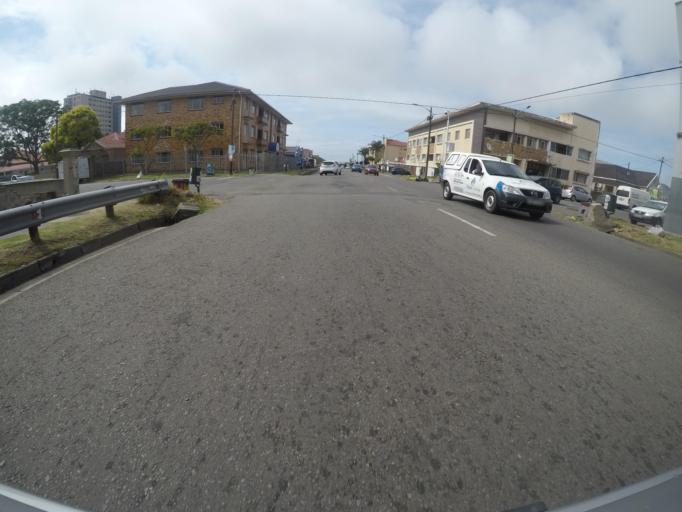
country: ZA
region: Eastern Cape
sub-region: Buffalo City Metropolitan Municipality
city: East London
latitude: -32.9996
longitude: 27.9047
